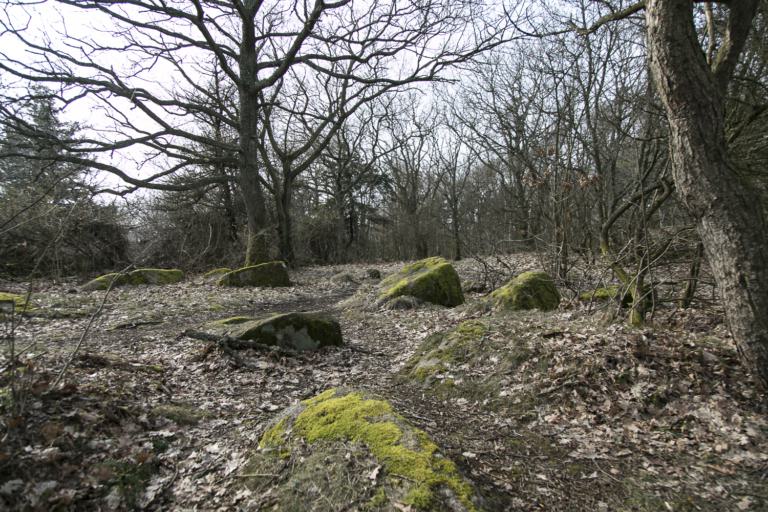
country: SE
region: Halland
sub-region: Varbergs Kommun
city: Varberg
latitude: 57.0838
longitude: 12.2468
